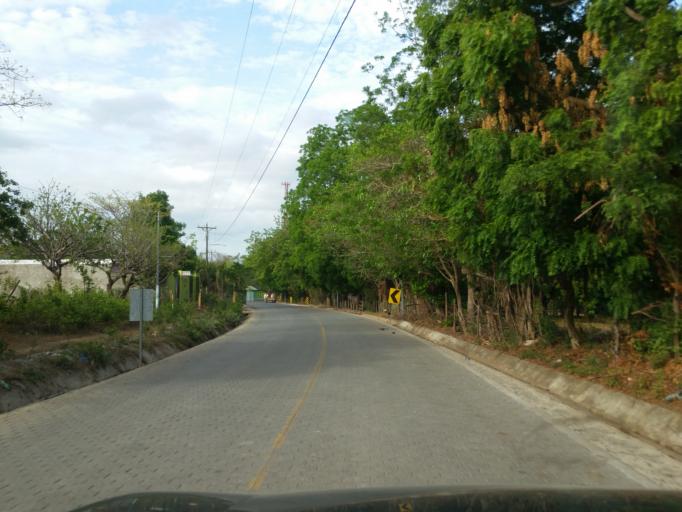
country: NI
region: Rivas
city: Tola
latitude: 11.4363
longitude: -85.9419
